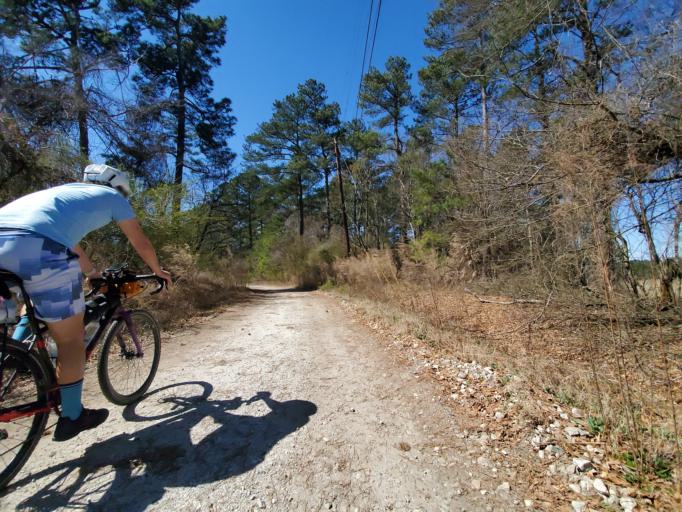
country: US
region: Georgia
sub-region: Barrow County
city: Winder
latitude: 33.9762
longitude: -83.7175
